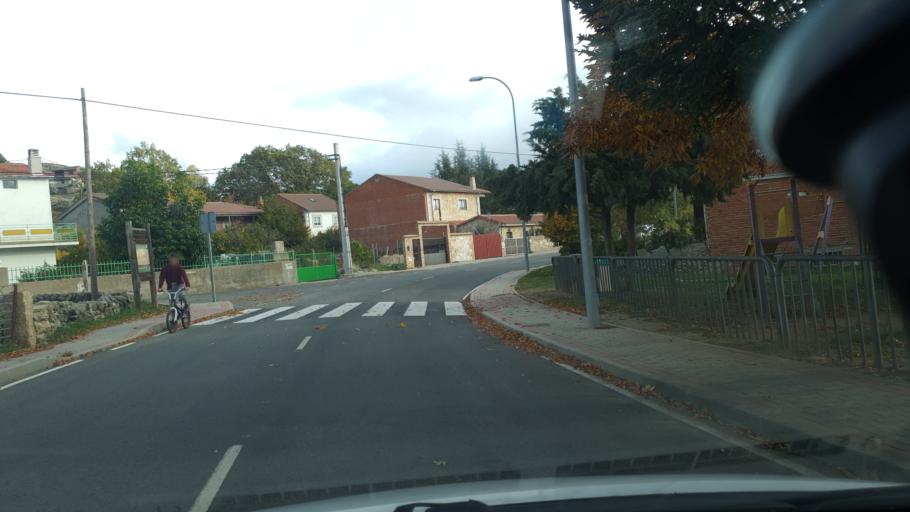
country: ES
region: Castille and Leon
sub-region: Provincia de Avila
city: Navalosa
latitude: 40.3996
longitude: -4.9311
